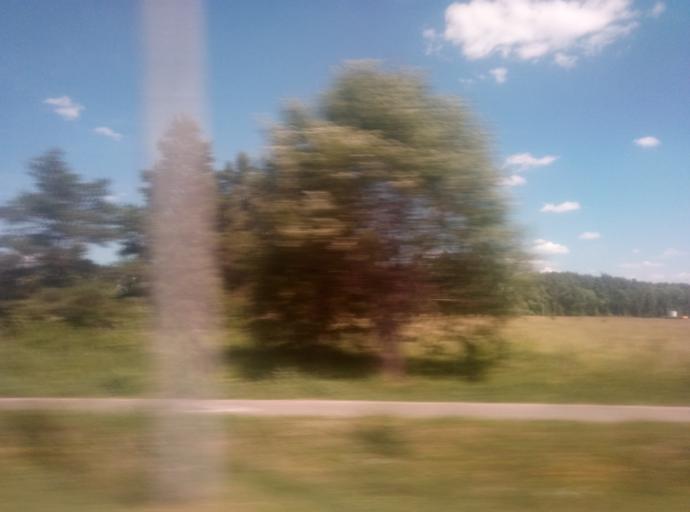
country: RU
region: Tula
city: Kireyevsk
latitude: 54.0187
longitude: 37.9094
